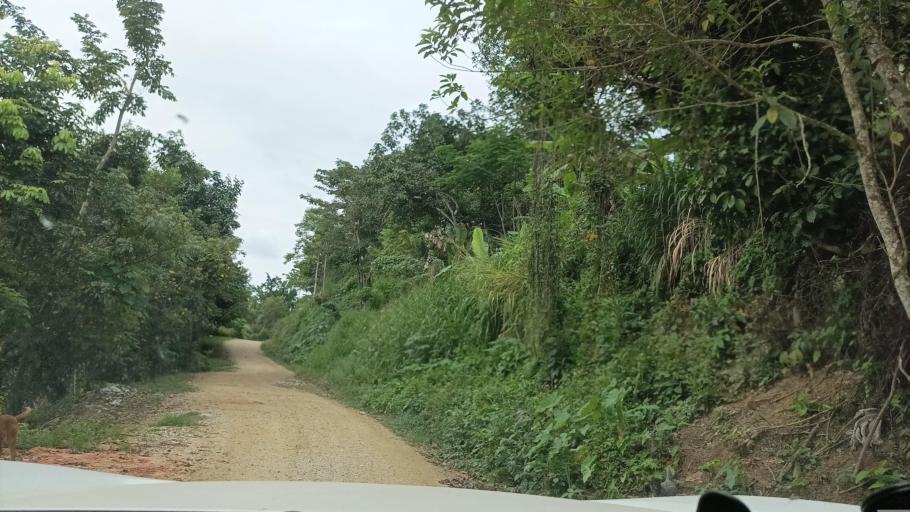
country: MX
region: Veracruz
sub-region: Uxpanapa
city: Poblado 10
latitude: 17.5692
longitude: -94.4239
